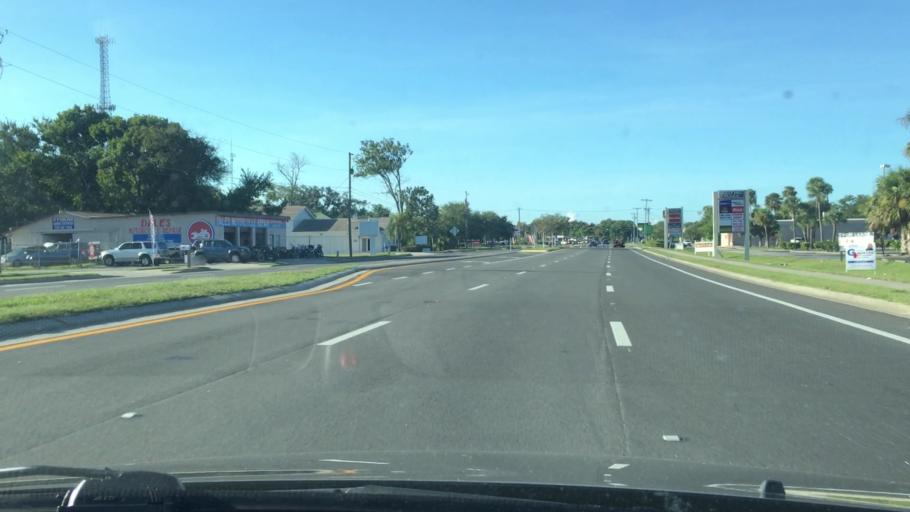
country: US
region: Florida
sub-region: Volusia County
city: Holly Hill
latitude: 29.2360
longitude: -81.0561
